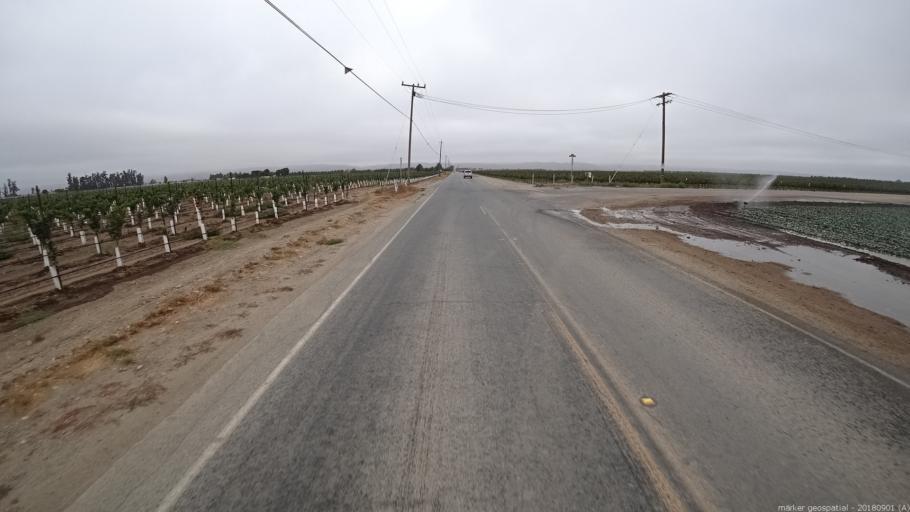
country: US
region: California
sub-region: Monterey County
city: Greenfield
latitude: 36.3023
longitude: -121.2683
